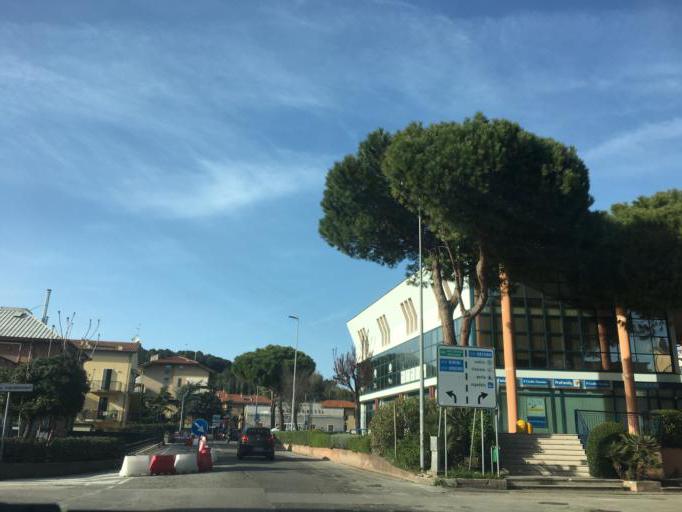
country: IT
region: The Marches
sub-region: Provincia di Pesaro e Urbino
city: Pesaro
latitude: 43.9098
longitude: 12.8970
